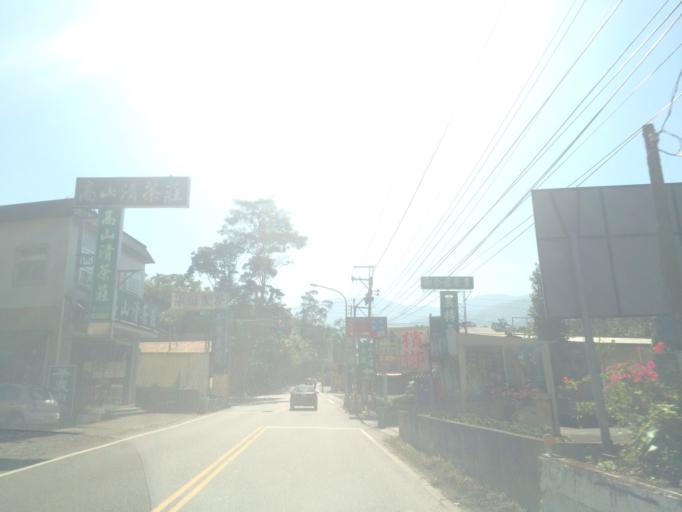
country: TW
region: Taiwan
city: Lugu
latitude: 23.7287
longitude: 120.7750
